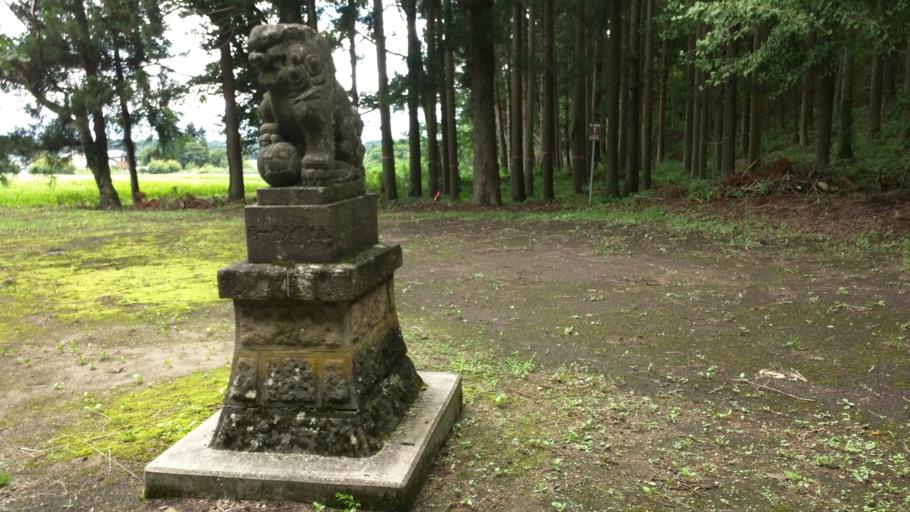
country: JP
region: Fukushima
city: Kitakata
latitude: 37.5829
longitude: 139.9448
